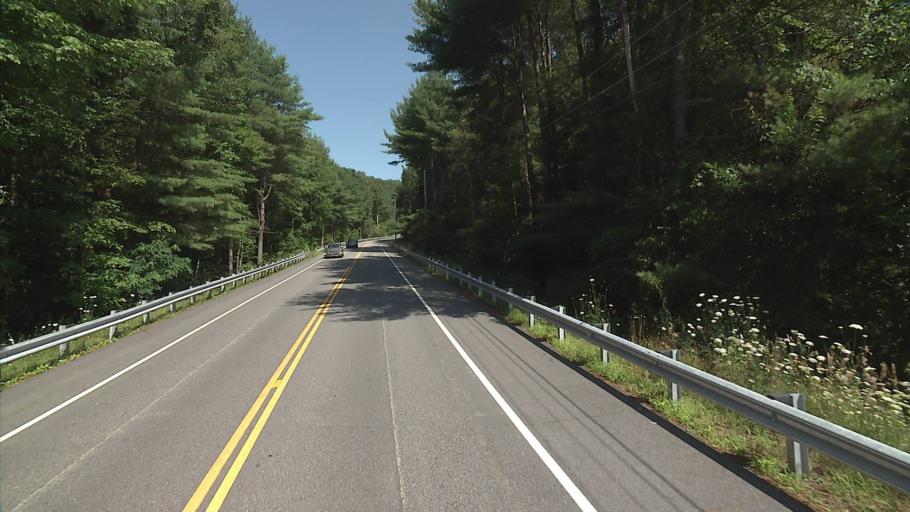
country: US
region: Connecticut
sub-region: Litchfield County
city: Winchester Center
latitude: 41.8679
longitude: -73.1688
